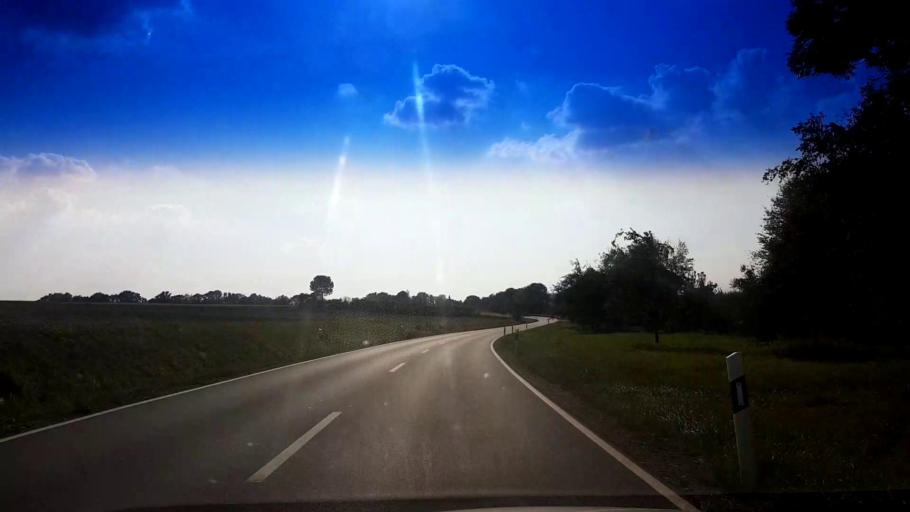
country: DE
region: Bavaria
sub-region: Upper Franconia
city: Schesslitz
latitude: 49.9615
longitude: 11.0105
